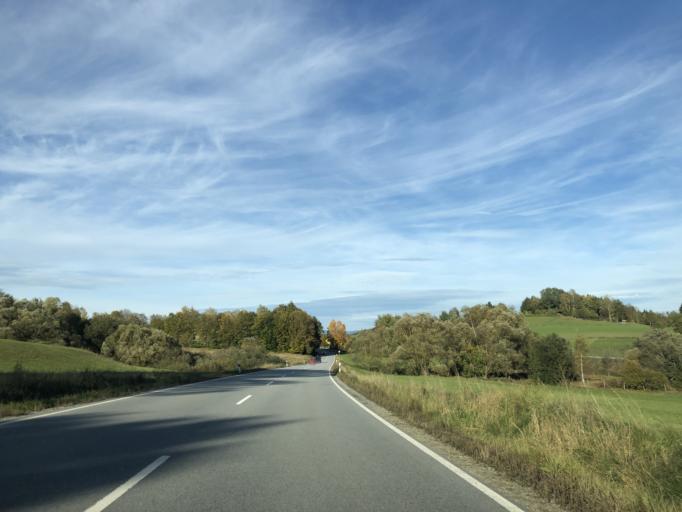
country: DE
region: Bavaria
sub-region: Lower Bavaria
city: Ruhmannsfelden
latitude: 48.9723
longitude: 12.9779
